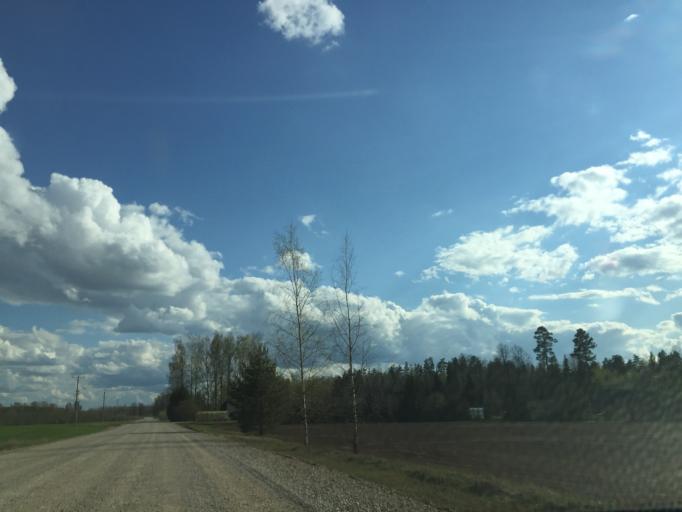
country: LV
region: Beverina
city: Murmuiza
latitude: 57.4114
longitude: 25.5118
